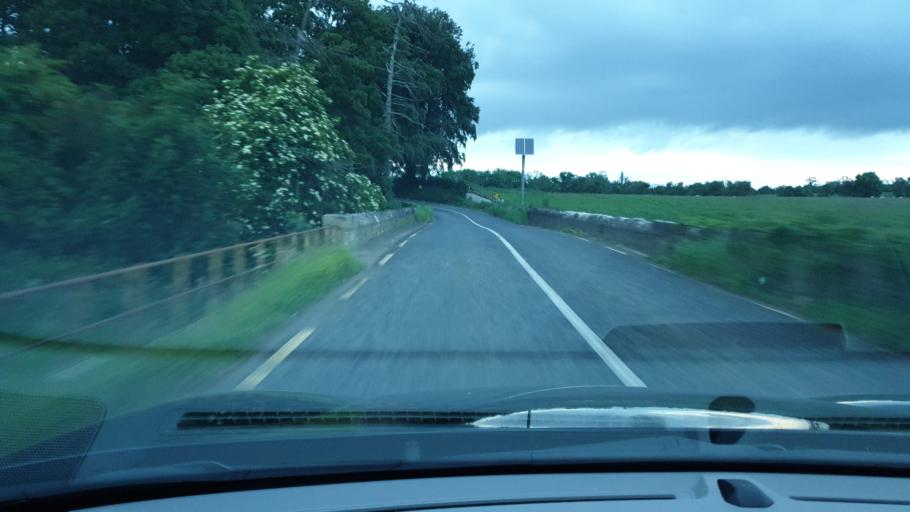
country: IE
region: Leinster
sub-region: An Mhi
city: Ashbourne
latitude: 53.4900
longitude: -6.3160
